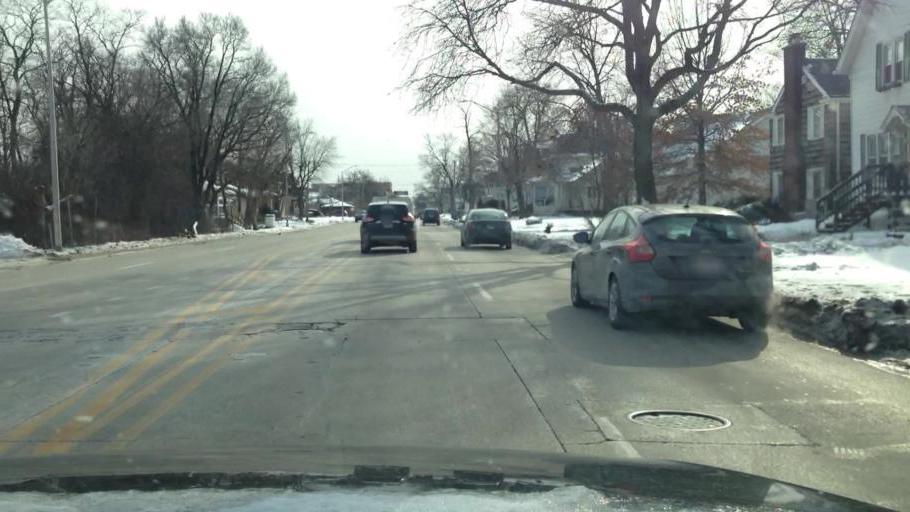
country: US
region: Illinois
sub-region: Cook County
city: Maywood
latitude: 41.8933
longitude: -87.8345
